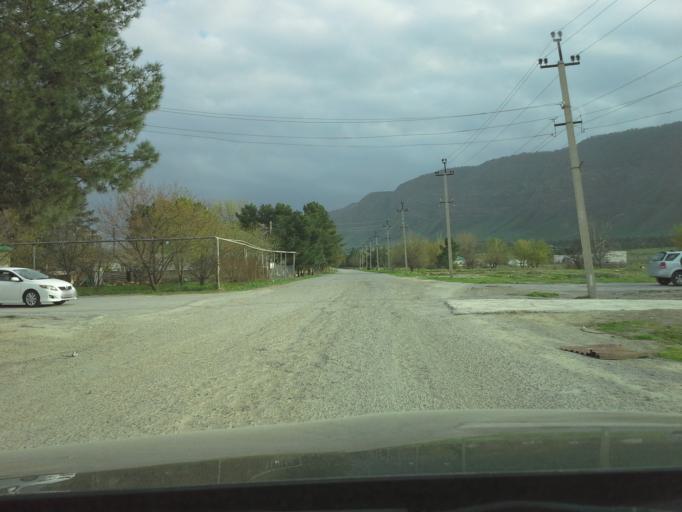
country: TM
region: Ahal
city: Abadan
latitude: 37.9326
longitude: 58.2276
